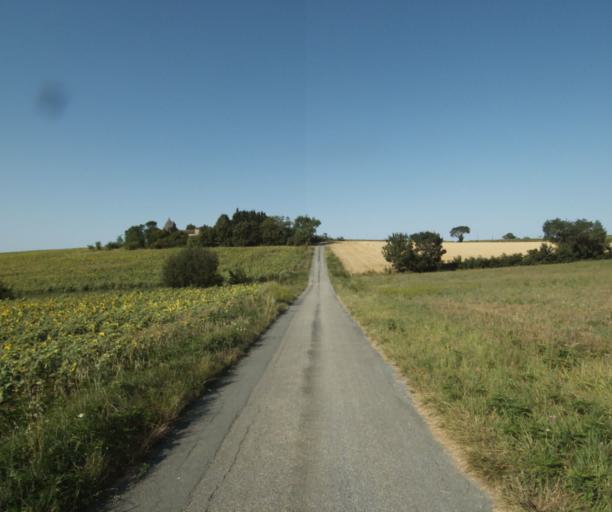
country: FR
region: Midi-Pyrenees
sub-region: Departement de la Haute-Garonne
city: Avignonet-Lauragais
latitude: 43.4278
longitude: 1.8139
